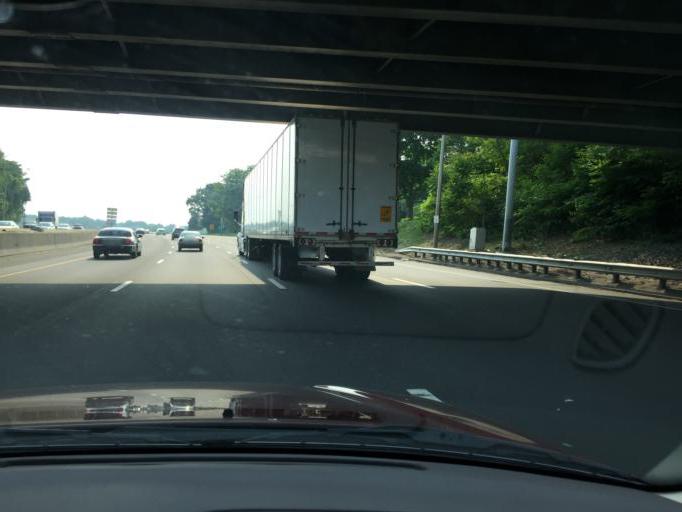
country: US
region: Connecticut
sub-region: Fairfield County
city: Darien
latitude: 41.0684
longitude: -73.4992
